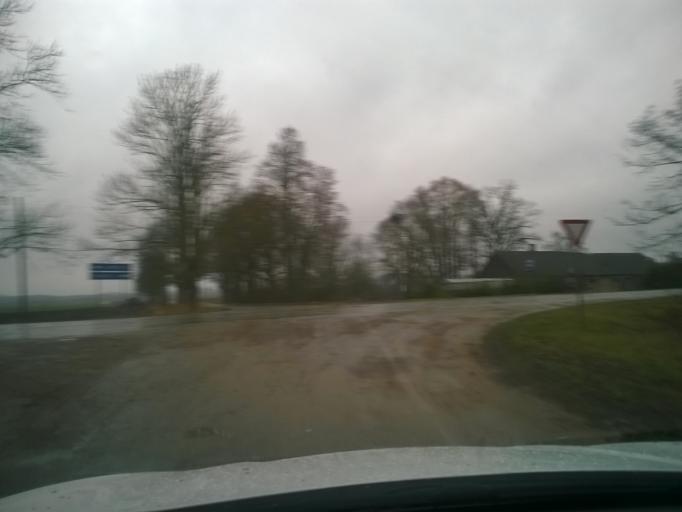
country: LV
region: Jaunpils
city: Jaunpils
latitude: 56.8484
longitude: 23.0448
